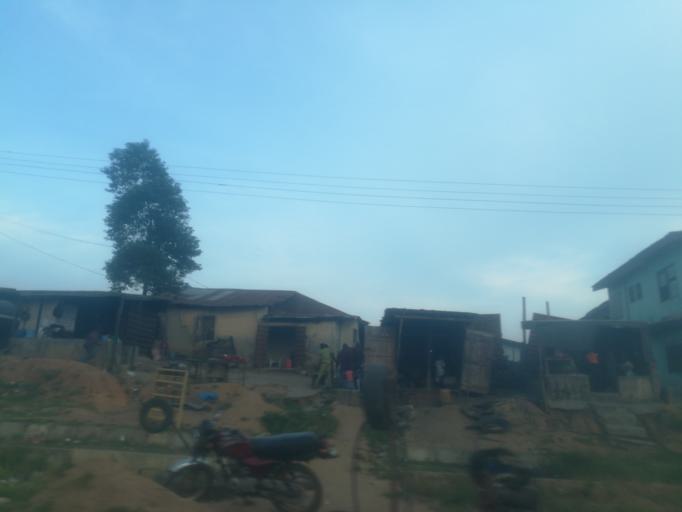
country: NG
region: Ogun
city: Abeokuta
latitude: 7.1758
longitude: 3.3397
